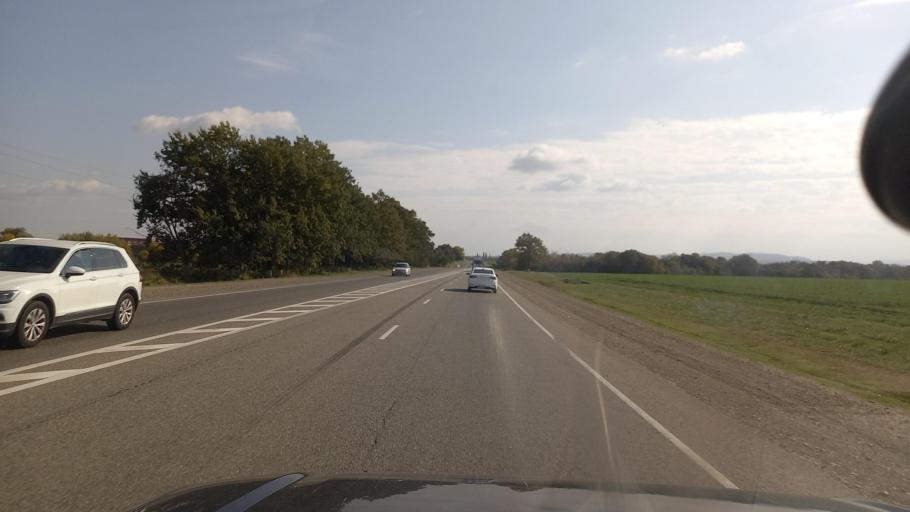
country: RU
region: Krasnodarskiy
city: Kholmskiy
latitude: 44.8548
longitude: 38.3513
